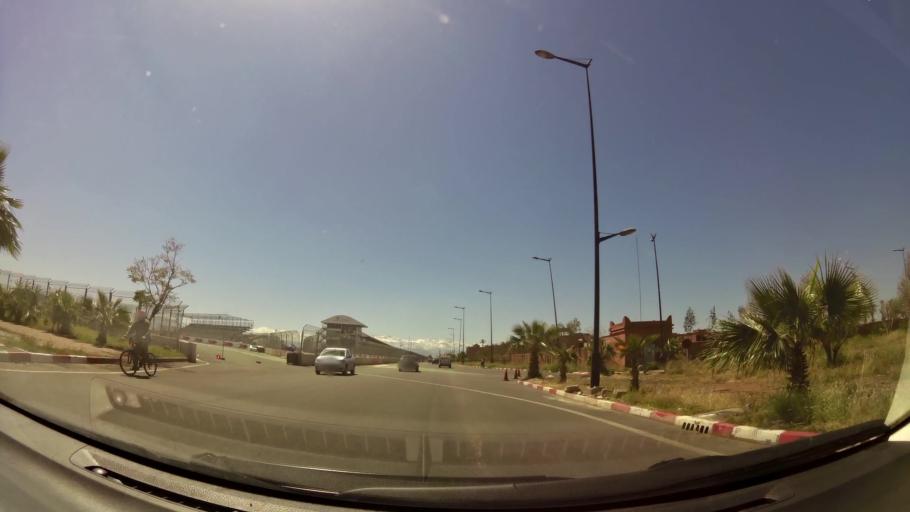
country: MA
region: Marrakech-Tensift-Al Haouz
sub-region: Marrakech
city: Marrakesh
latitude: 31.5827
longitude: -7.9832
